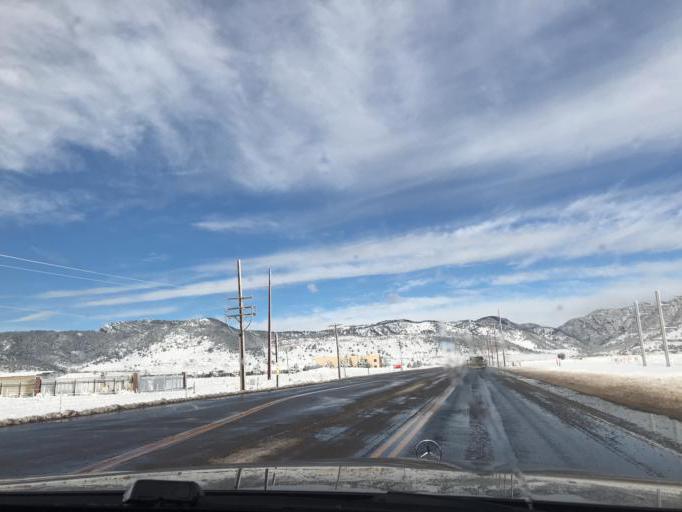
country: US
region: Colorado
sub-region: Boulder County
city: Superior
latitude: 39.8648
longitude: -105.2255
